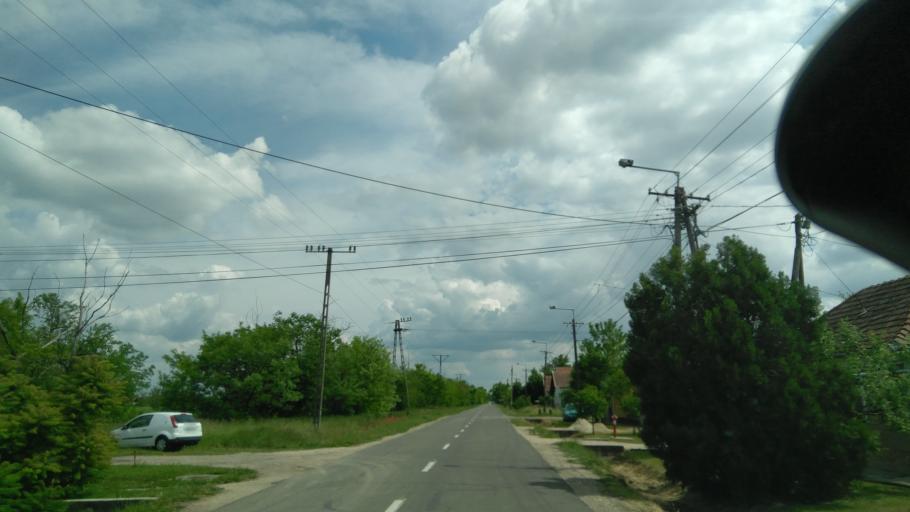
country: HU
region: Bekes
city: Totkomlos
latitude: 46.4043
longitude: 20.7471
